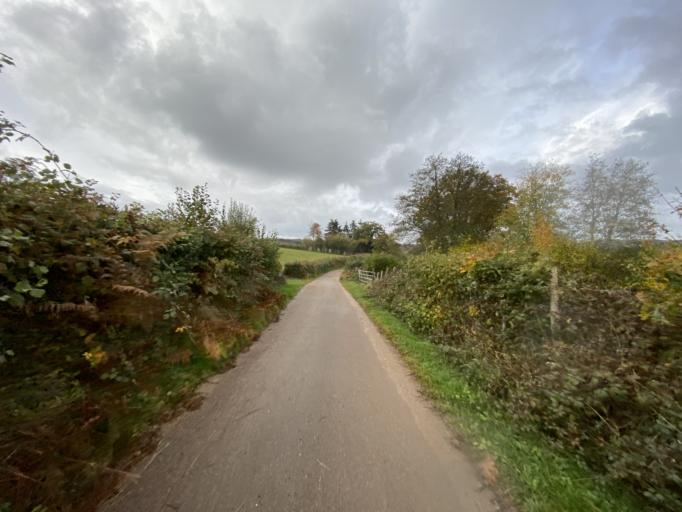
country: FR
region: Bourgogne
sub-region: Departement de la Cote-d'Or
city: Saulieu
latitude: 47.2950
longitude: 4.1192
